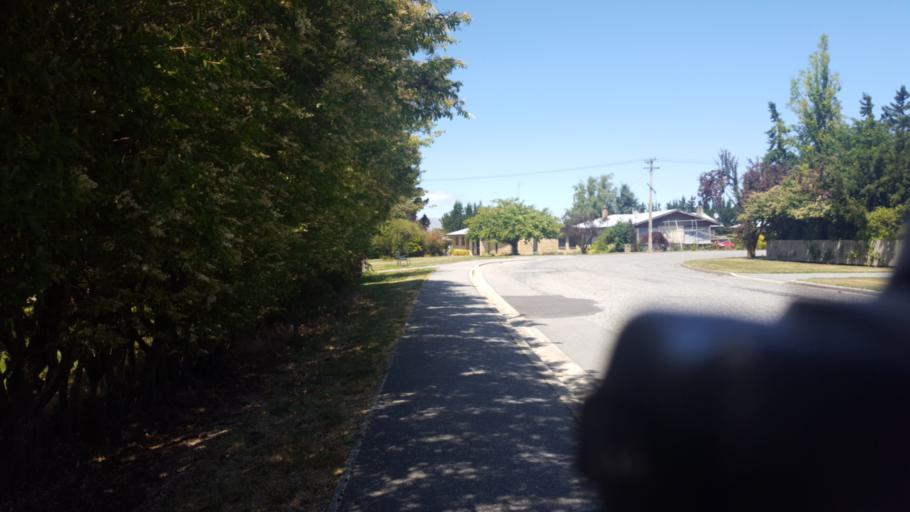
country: NZ
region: Otago
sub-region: Dunedin City
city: Dunedin
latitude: -45.1279
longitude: 170.1092
